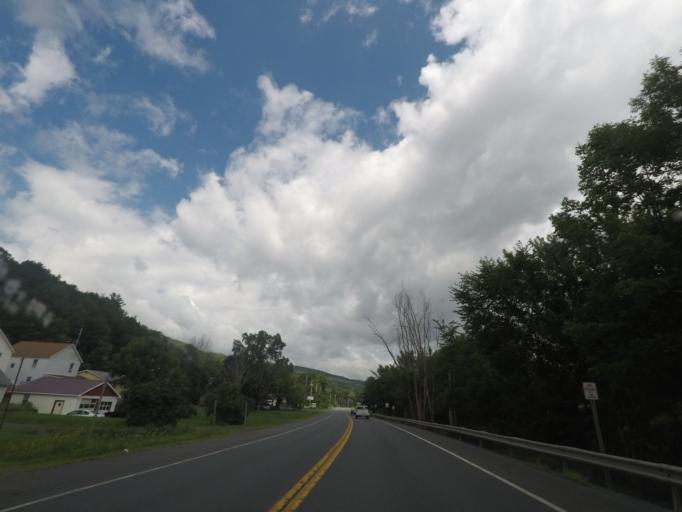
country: US
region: Massachusetts
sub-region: Berkshire County
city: Williamstown
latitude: 42.6904
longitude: -73.3698
